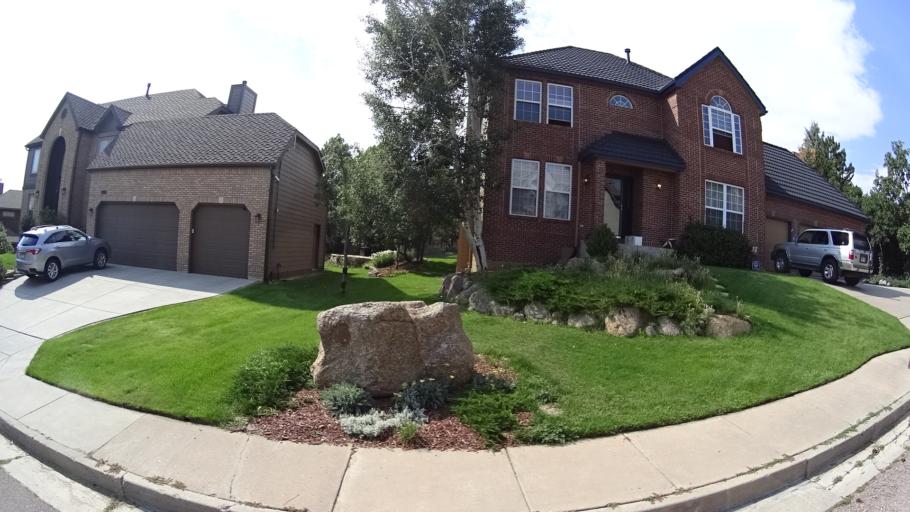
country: US
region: Colorado
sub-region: El Paso County
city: Fort Carson
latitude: 38.7459
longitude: -104.8341
